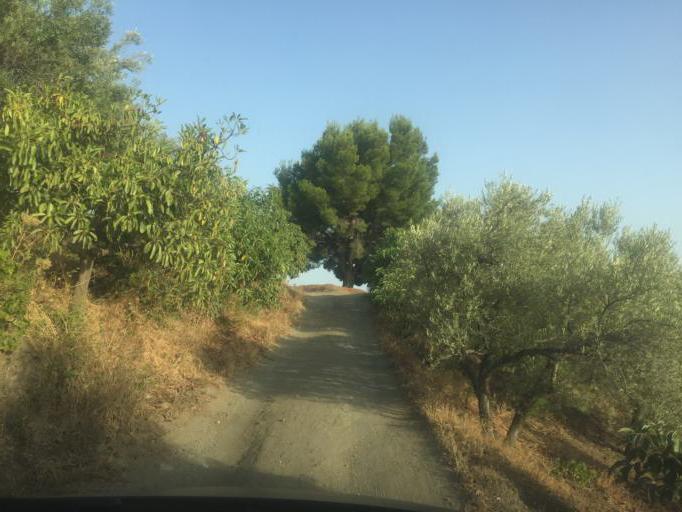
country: ES
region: Andalusia
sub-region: Provincia de Malaga
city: Frigiliana
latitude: 36.8075
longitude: -3.9313
